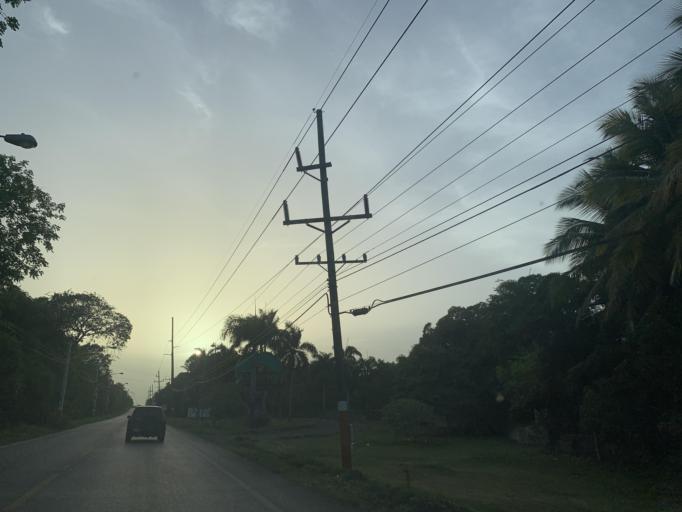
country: DO
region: Puerto Plata
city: Cabarete
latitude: 19.7766
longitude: -70.4702
